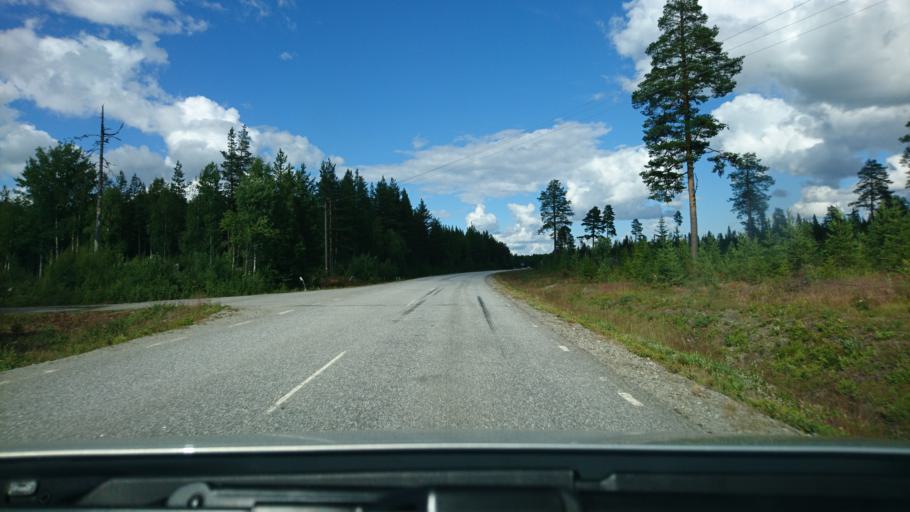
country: SE
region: Vaesterbotten
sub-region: Asele Kommun
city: Asele
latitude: 63.9998
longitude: 17.2675
